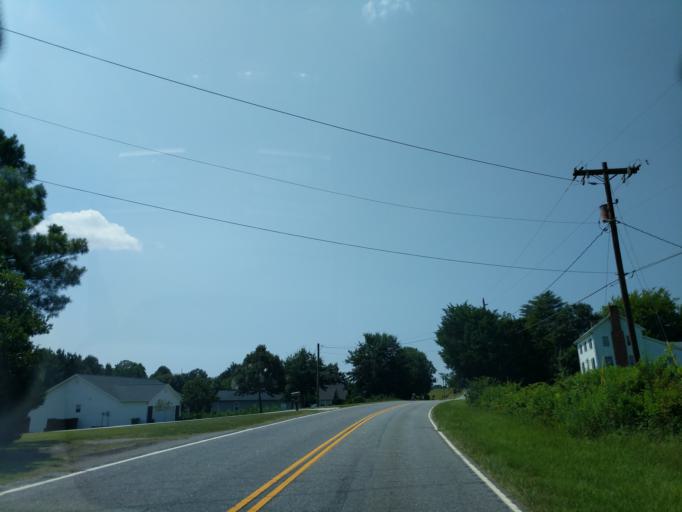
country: US
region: South Carolina
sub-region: Spartanburg County
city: Duncan
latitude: 34.9603
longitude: -82.1826
